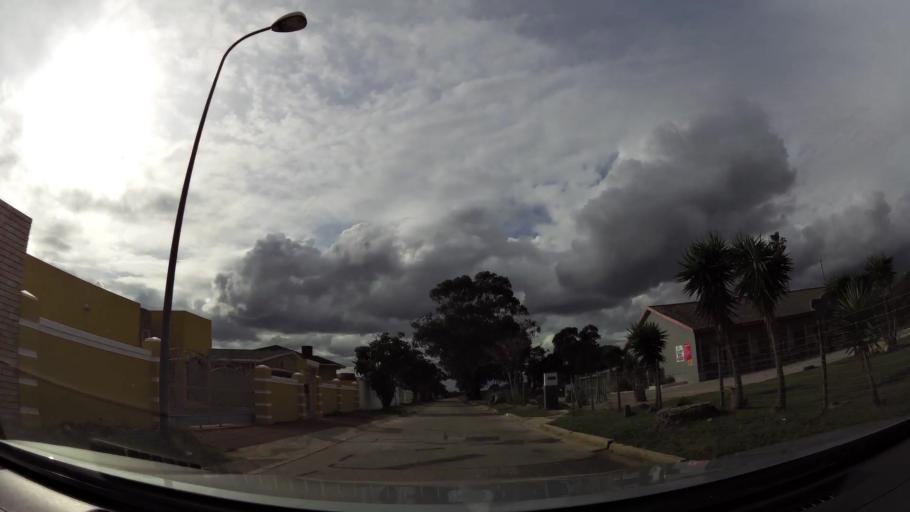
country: ZA
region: Eastern Cape
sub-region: Nelson Mandela Bay Metropolitan Municipality
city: Port Elizabeth
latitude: -33.9407
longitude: 25.5058
